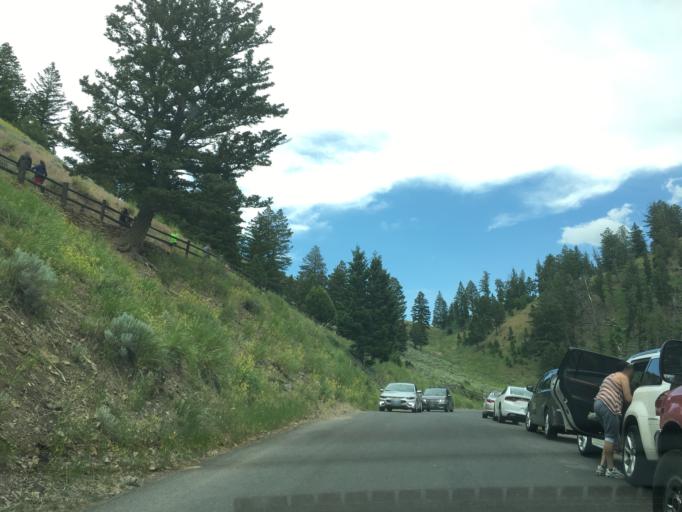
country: US
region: Montana
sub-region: Gallatin County
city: West Yellowstone
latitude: 44.9162
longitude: -110.4397
